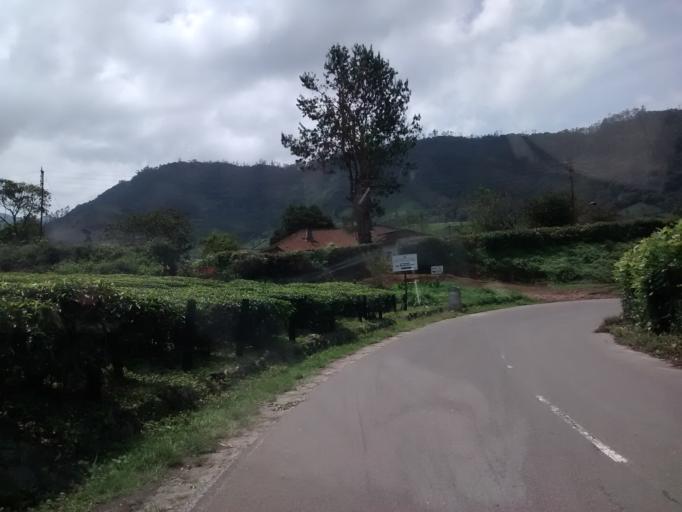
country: IN
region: Kerala
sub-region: Idukki
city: Munnar
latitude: 10.1054
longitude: 77.1192
